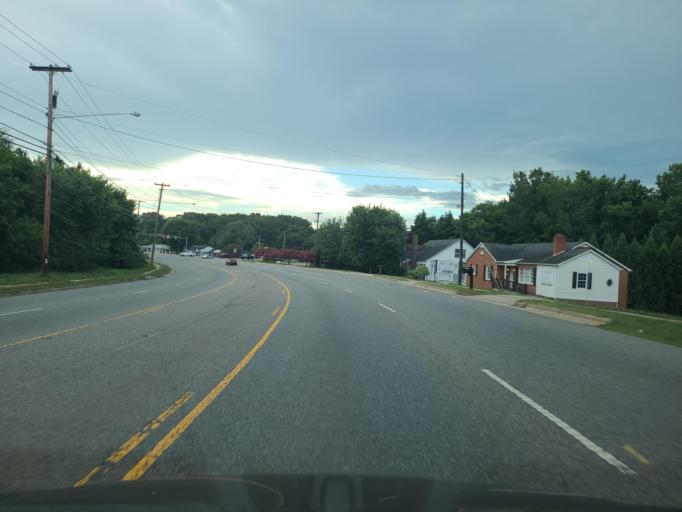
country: US
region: North Carolina
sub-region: Gaston County
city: Ranlo
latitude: 35.2852
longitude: -81.1493
